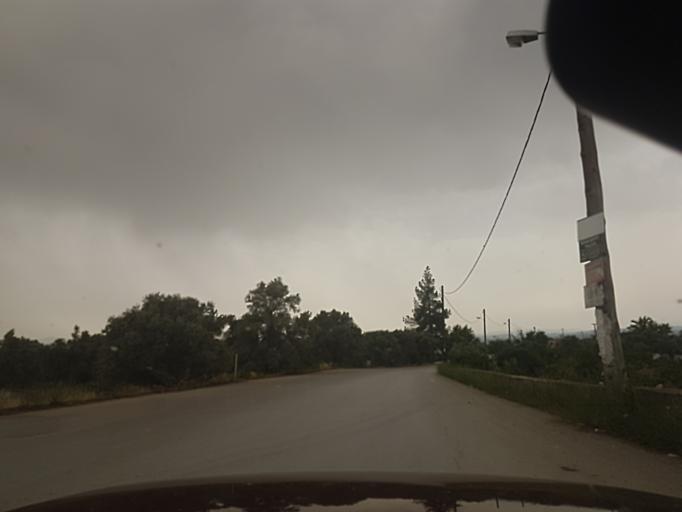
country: GR
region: Central Greece
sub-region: Nomos Evvoias
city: Filla
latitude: 38.4418
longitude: 23.6728
